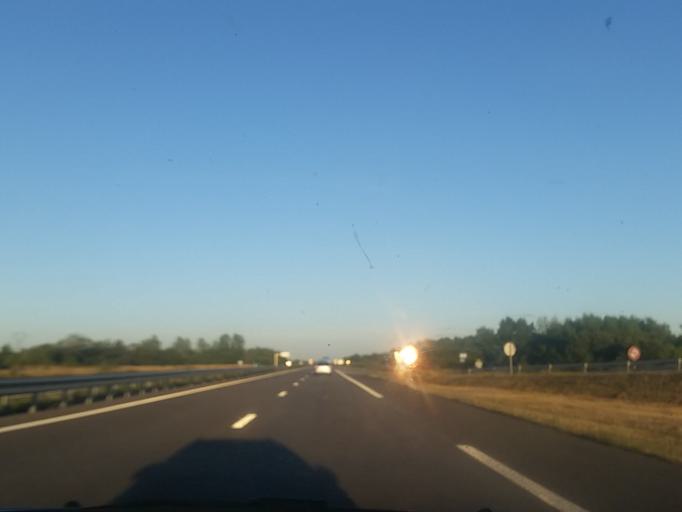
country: FR
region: Pays de la Loire
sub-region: Departement de la Loire-Atlantique
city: Saint-Jean-de-Boiseau
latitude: 47.1834
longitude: -1.7237
